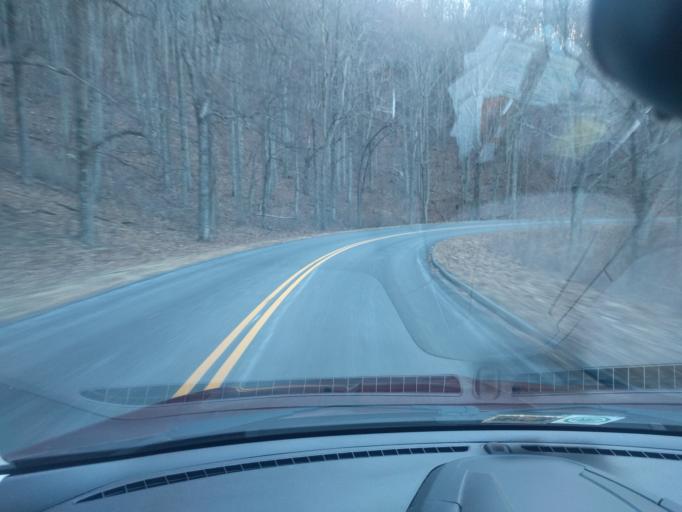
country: US
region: Virginia
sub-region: Botetourt County
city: Buchanan
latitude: 37.4796
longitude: -79.6542
